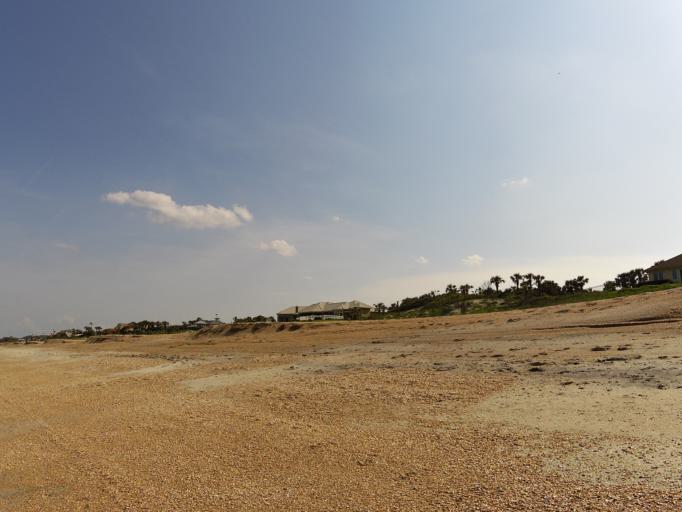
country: US
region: Florida
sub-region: Saint Johns County
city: Palm Valley
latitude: 30.1532
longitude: -81.3533
